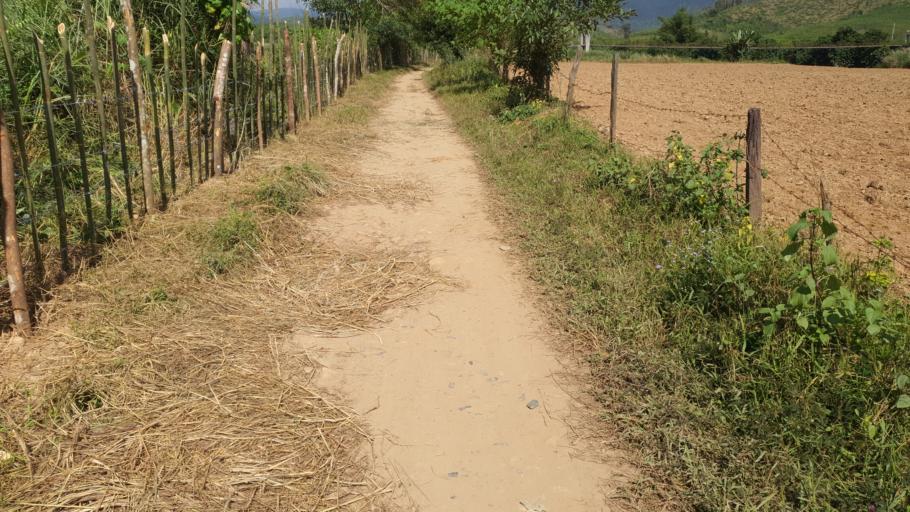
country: LA
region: Bolikhamxai
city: Bolikhan
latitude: 18.9074
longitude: 103.7430
